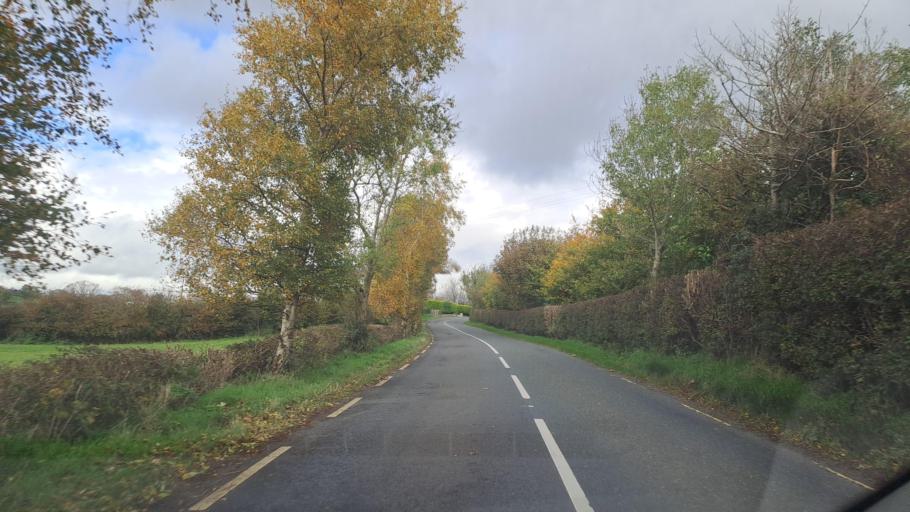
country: IE
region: Ulster
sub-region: An Cabhan
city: Mullagh
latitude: 53.8138
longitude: -6.9491
